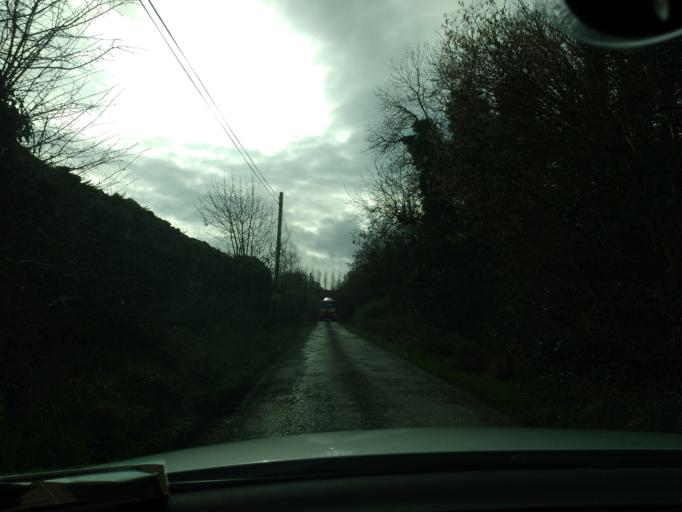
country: IE
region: Leinster
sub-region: Laois
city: Rathdowney
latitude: 52.6654
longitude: -7.5686
